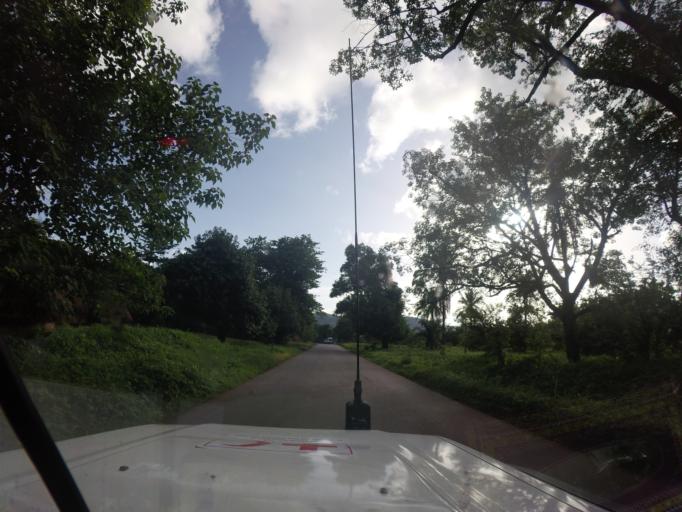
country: GN
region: Kindia
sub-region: Kindia
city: Kindia
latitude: 10.0043
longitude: -12.7785
